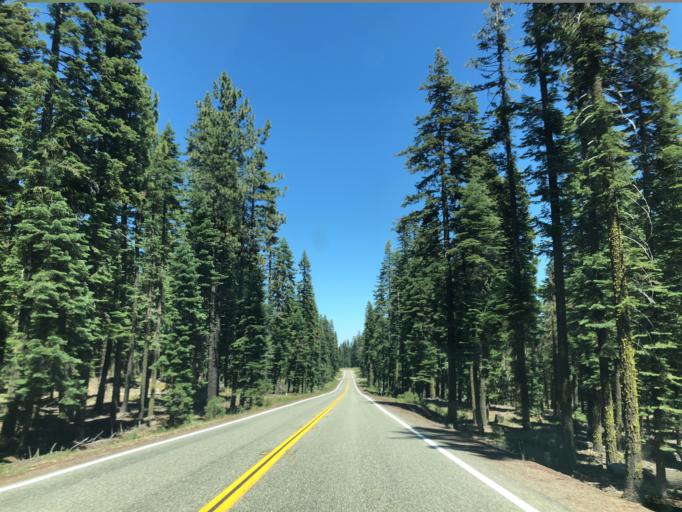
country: US
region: California
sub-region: Shasta County
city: Burney
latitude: 40.5887
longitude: -121.5460
